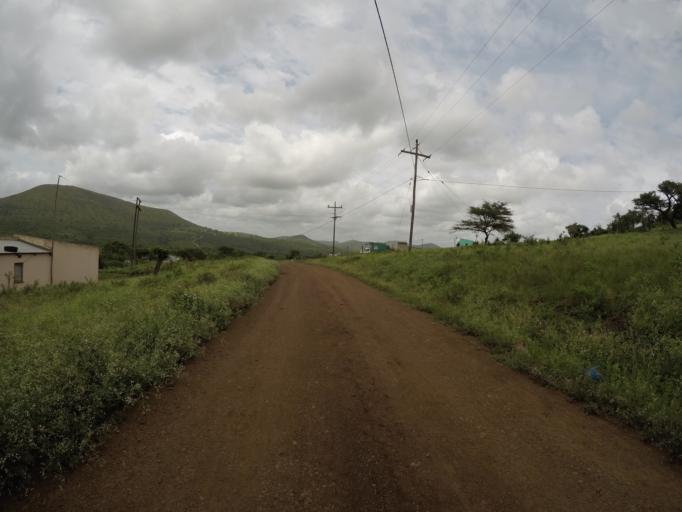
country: ZA
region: KwaZulu-Natal
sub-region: uThungulu District Municipality
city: Empangeni
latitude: -28.5884
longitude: 31.8886
